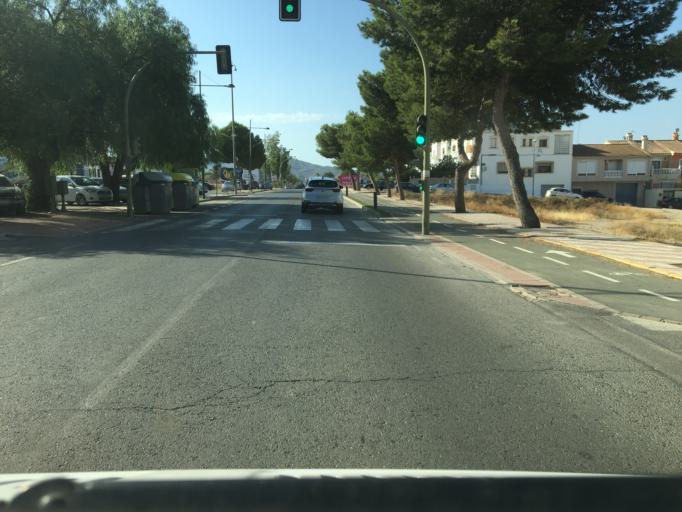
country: ES
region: Andalusia
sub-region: Provincia de Almeria
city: Huercal-Overa
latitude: 37.4027
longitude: -1.9543
